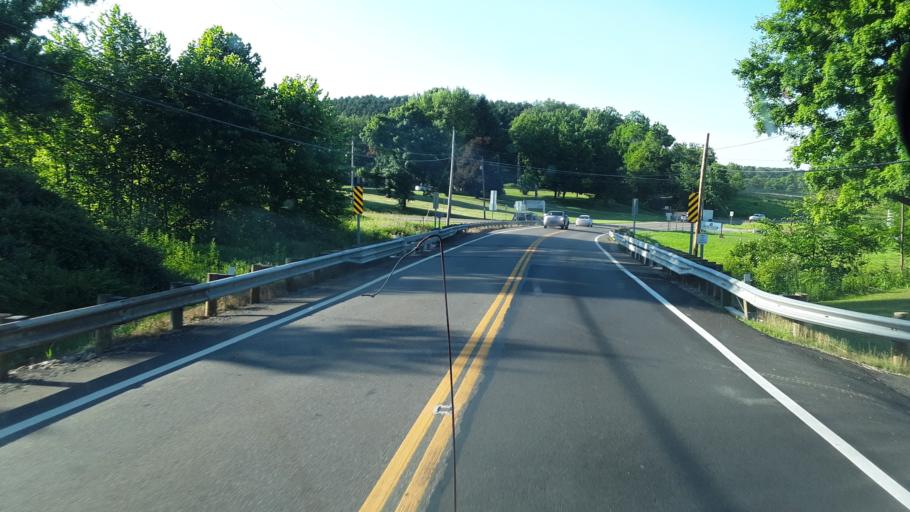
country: US
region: Ohio
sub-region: Tuscarawas County
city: Rockford
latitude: 40.5044
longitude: -81.2442
